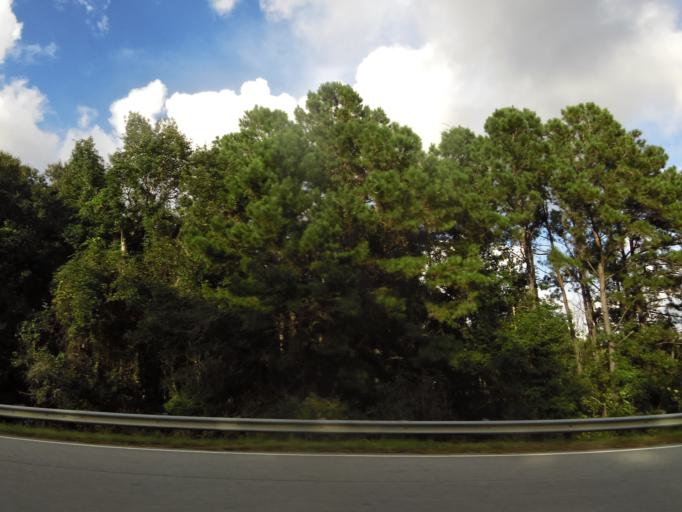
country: US
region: Georgia
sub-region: Liberty County
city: Midway
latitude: 31.7337
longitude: -81.4312
